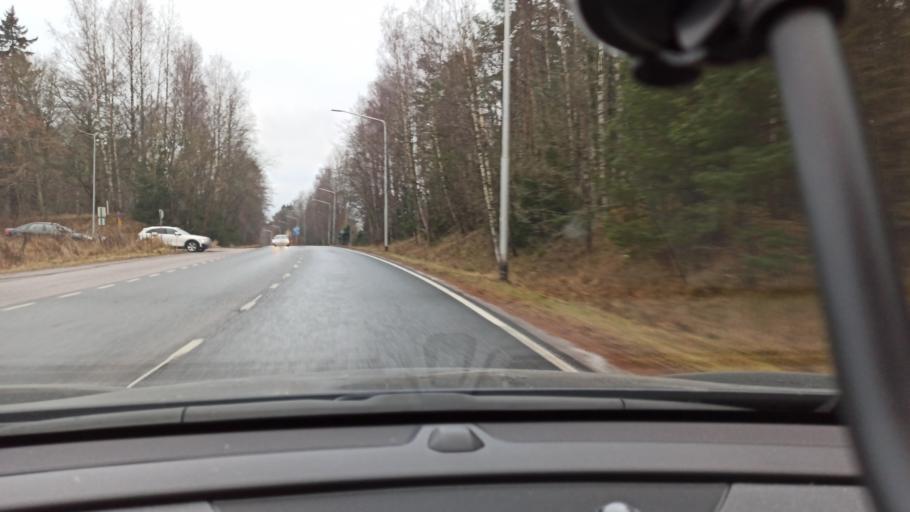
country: FI
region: Uusimaa
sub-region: Helsinki
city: Kirkkonummi
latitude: 60.1381
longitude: 24.4475
